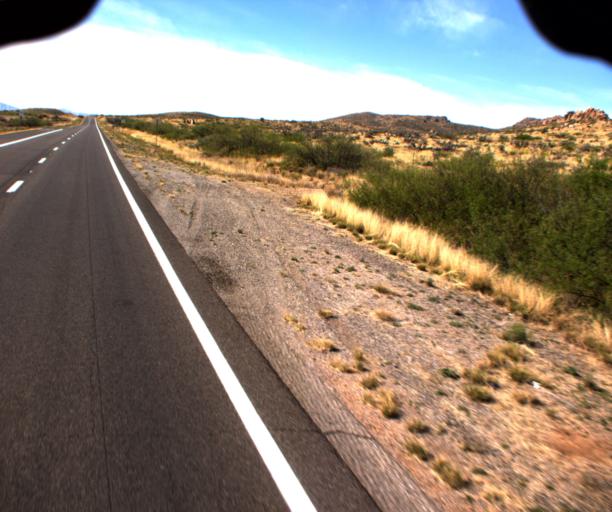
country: US
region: Arizona
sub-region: Graham County
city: Swift Trail Junction
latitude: 32.5242
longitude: -109.6740
